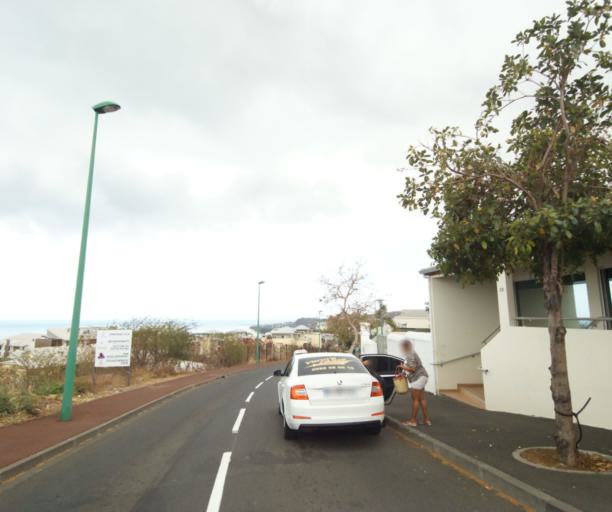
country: RE
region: Reunion
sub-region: Reunion
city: Saint-Paul
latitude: -21.0651
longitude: 55.2278
